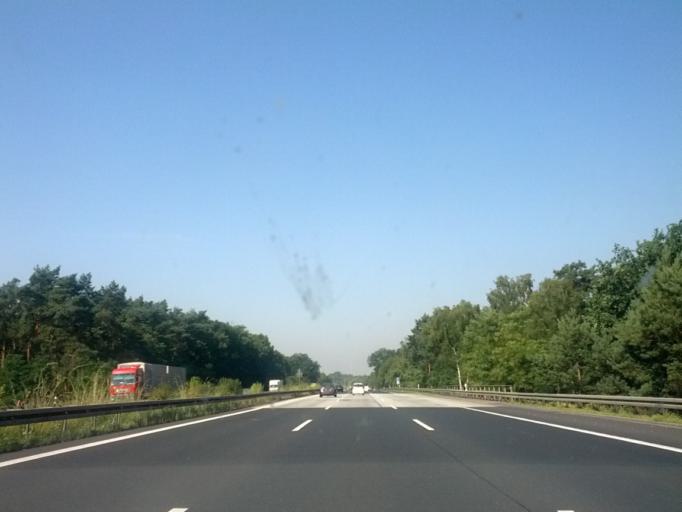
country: DE
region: Brandenburg
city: Rangsdorf
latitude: 52.3070
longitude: 13.3856
